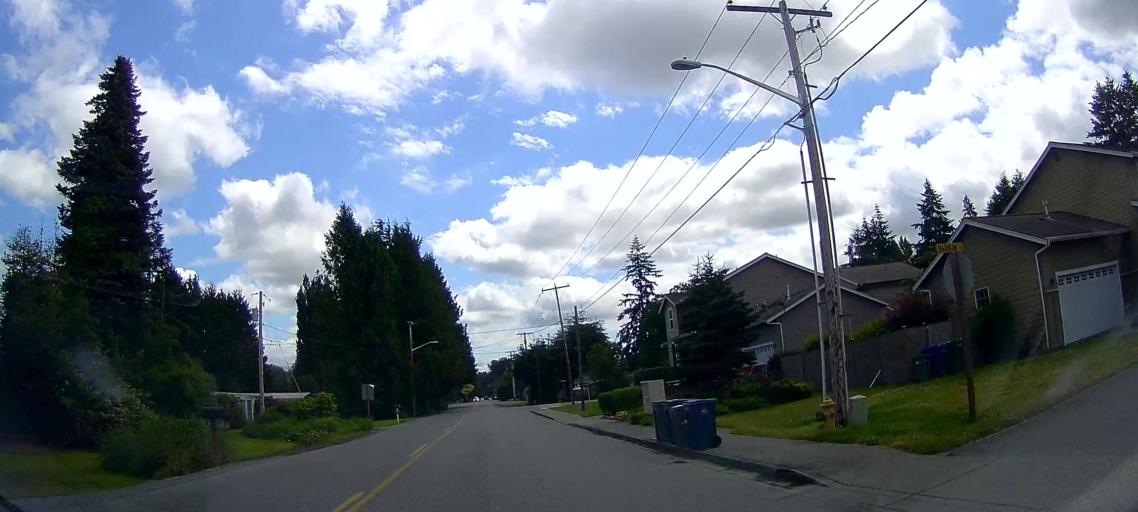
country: US
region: Washington
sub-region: Skagit County
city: Burlington
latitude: 48.4760
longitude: -122.3085
